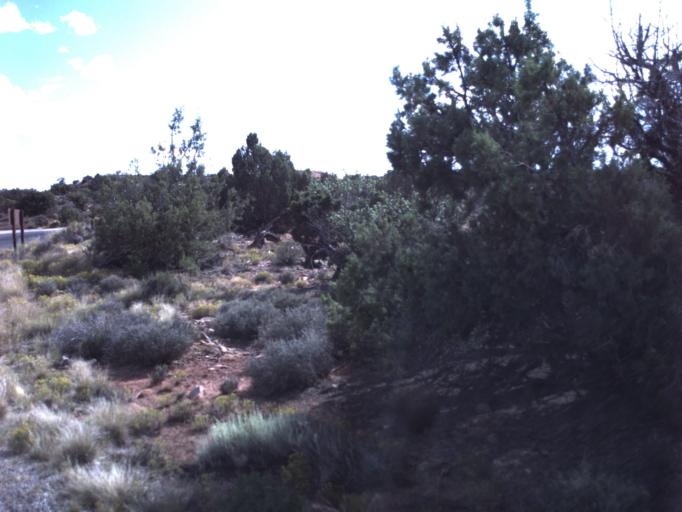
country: US
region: Utah
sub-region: Grand County
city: Moab
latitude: 38.4881
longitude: -109.7365
